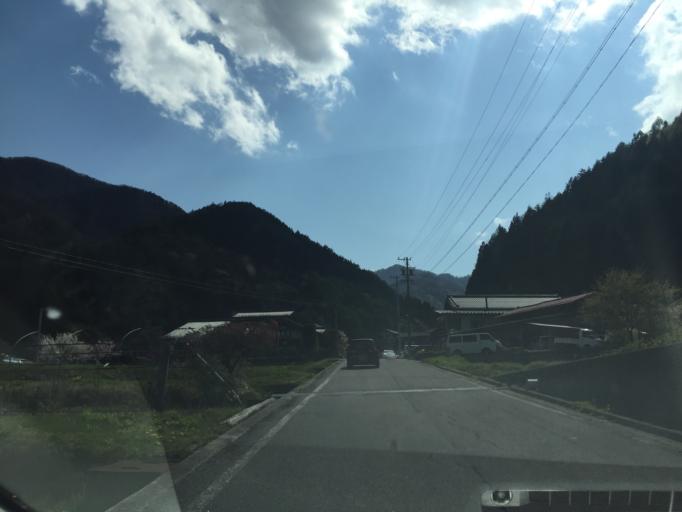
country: JP
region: Gifu
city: Nakatsugawa
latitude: 35.4393
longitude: 137.6511
